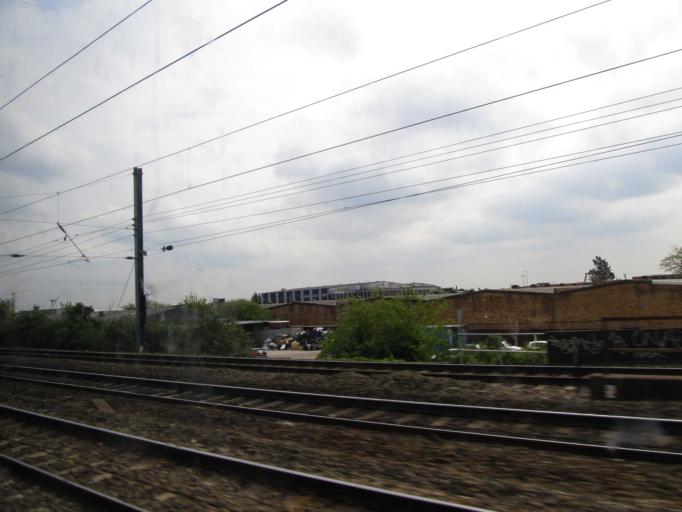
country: GB
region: England
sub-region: Greater London
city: Hayes
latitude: 51.5030
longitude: -0.4040
